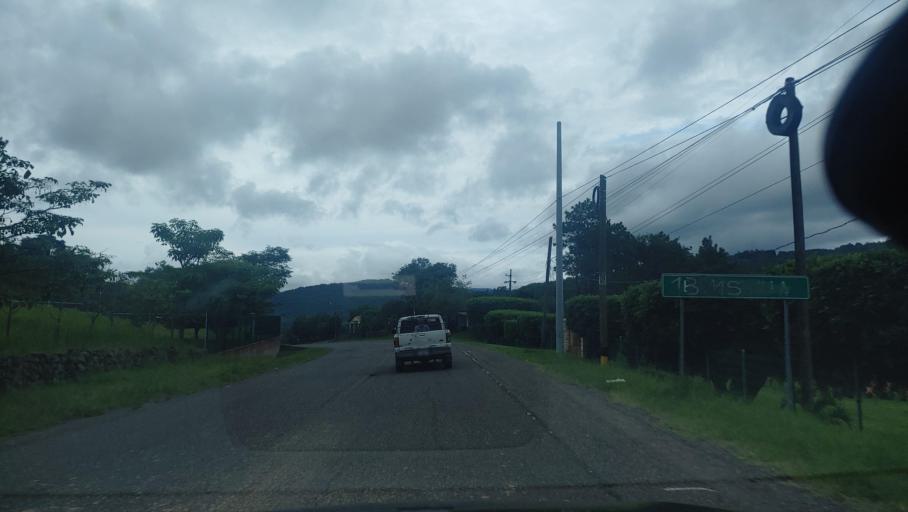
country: HN
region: Choluteca
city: San Marcos de Colon
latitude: 13.3756
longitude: -86.8930
